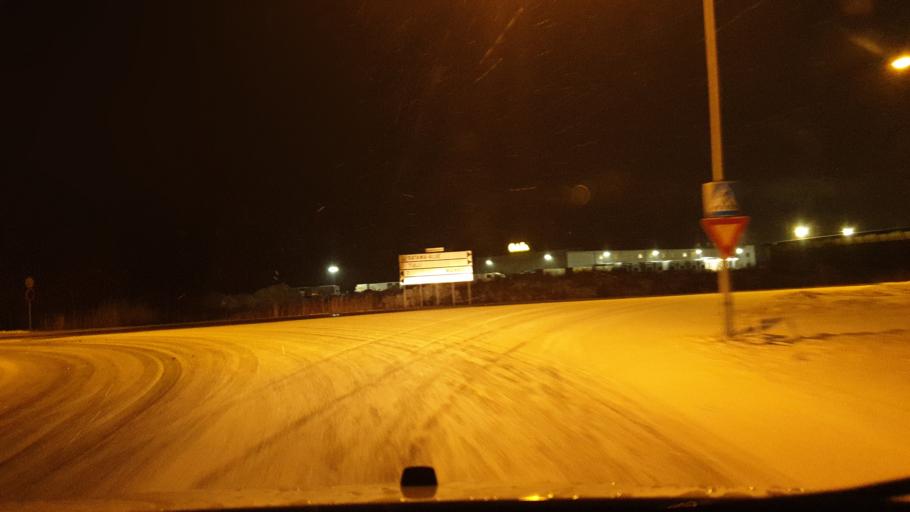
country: FI
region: Northern Ostrobothnia
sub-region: Oulu
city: Oulu
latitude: 64.9899
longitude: 25.4344
